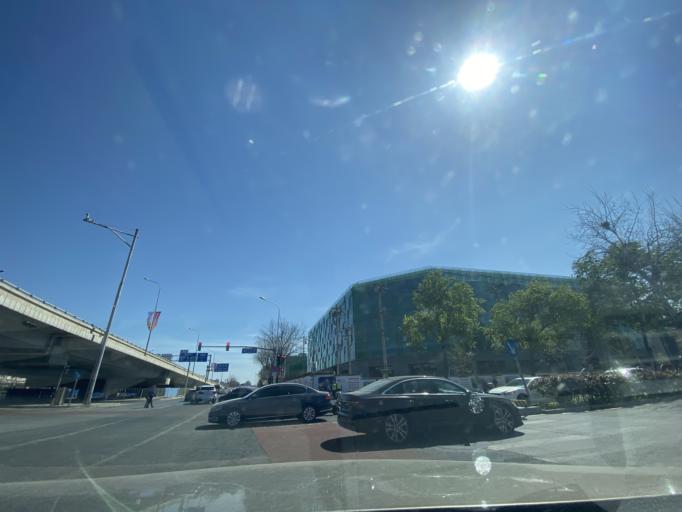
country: CN
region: Beijing
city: Sijiqing
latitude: 39.9227
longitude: 116.2584
